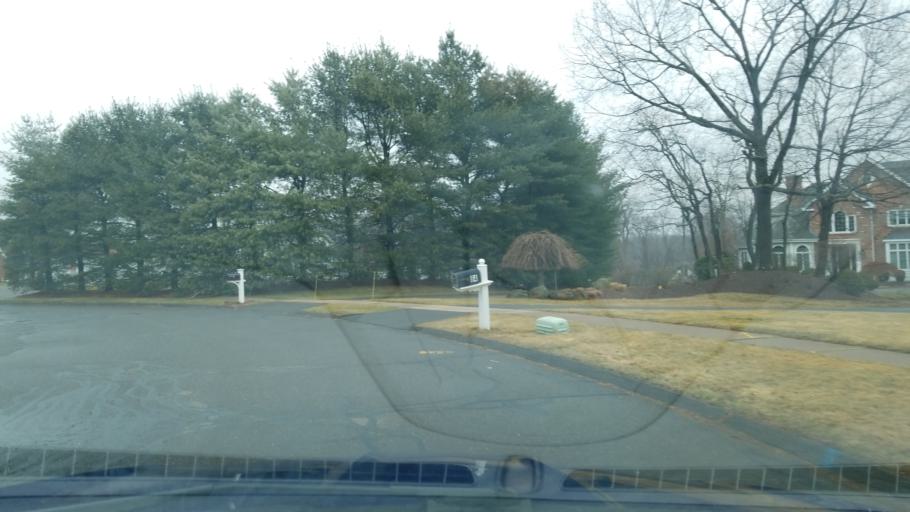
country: US
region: Connecticut
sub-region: Hartford County
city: Newington
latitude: 41.6735
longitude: -72.7000
